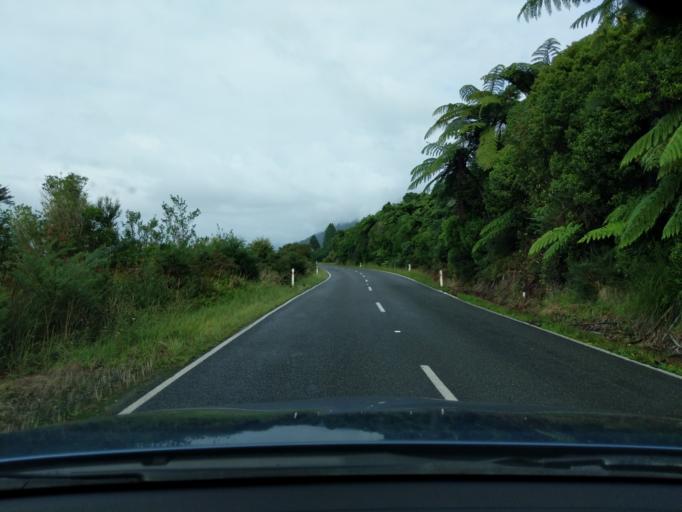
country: NZ
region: Tasman
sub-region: Tasman District
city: Takaka
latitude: -40.6410
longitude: 172.6654
